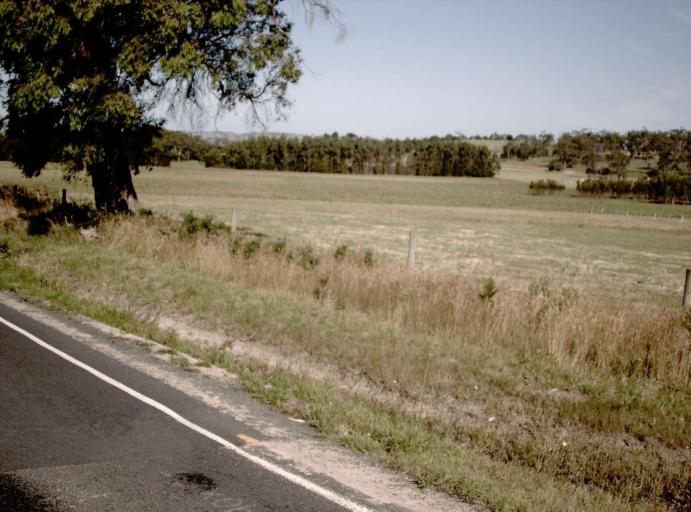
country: AU
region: Victoria
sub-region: Baw Baw
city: Warragul
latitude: -38.5538
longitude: 146.0512
